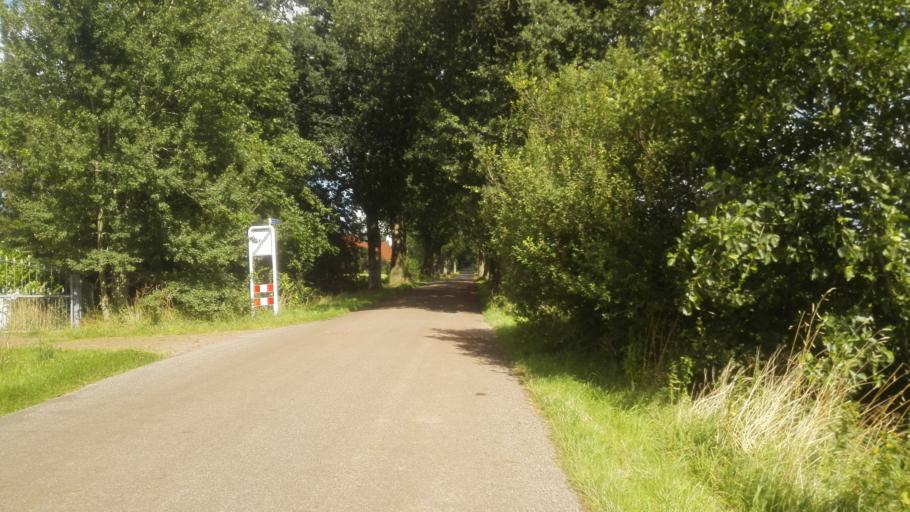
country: NL
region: Friesland
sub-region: Gemeente Heerenveen
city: Nieuwehorne
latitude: 52.9265
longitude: 6.0965
